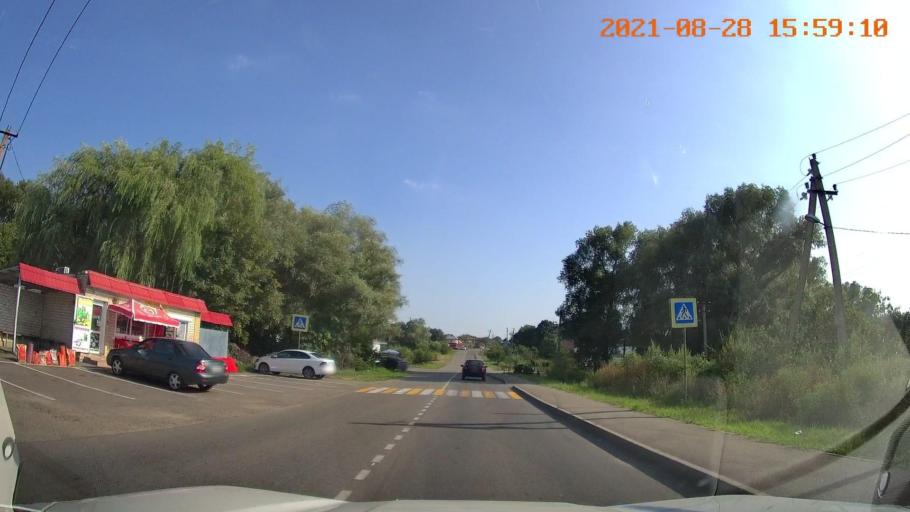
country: RU
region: Stavropol'skiy
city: Tatarka
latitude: 44.9609
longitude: 41.9617
